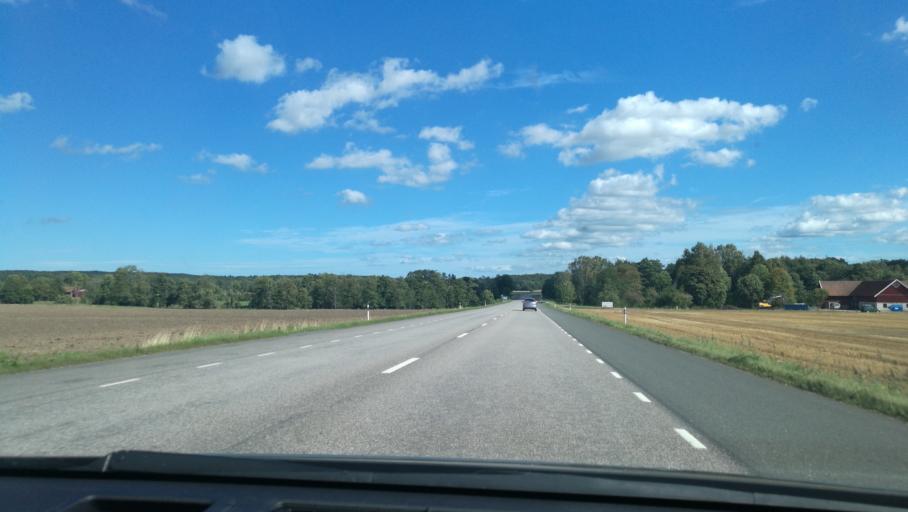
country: SE
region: Vaestra Goetaland
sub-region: Gotene Kommun
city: Kallby
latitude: 58.5072
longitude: 13.3193
